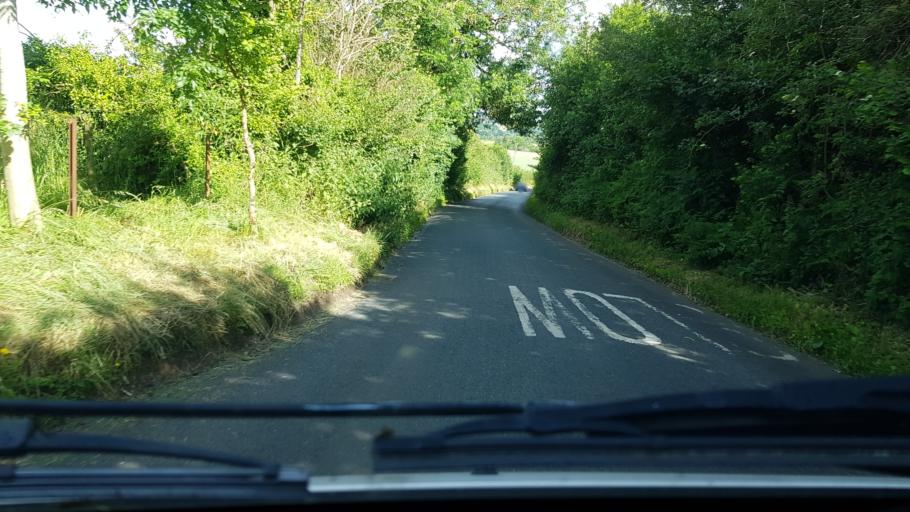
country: GB
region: England
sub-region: Worcestershire
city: Bewdley
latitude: 52.3902
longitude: -2.3058
